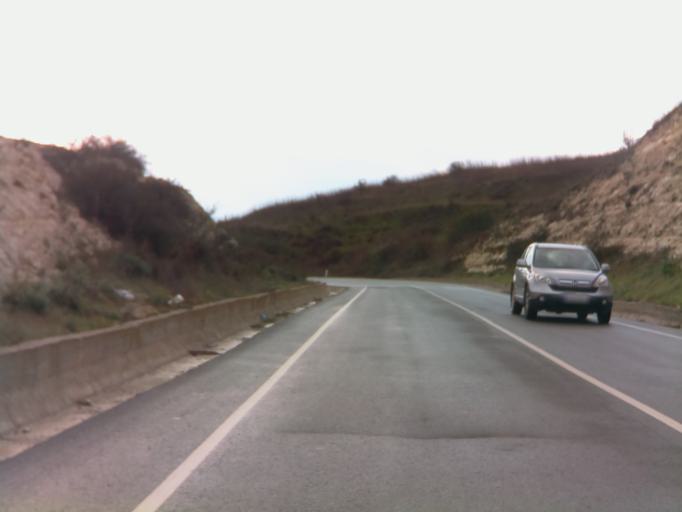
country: CY
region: Pafos
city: Pegeia
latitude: 34.9045
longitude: 32.4427
